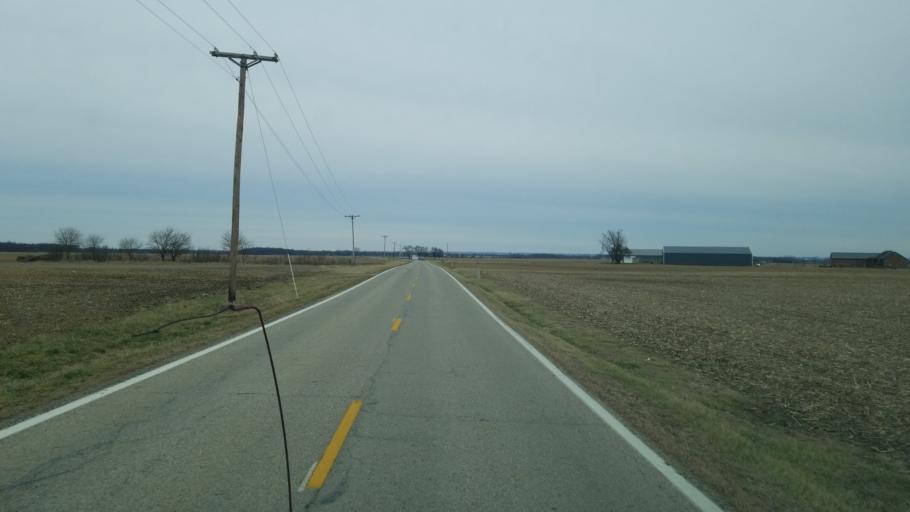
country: US
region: Ohio
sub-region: Pickaway County
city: Williamsport
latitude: 39.5561
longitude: -83.0980
